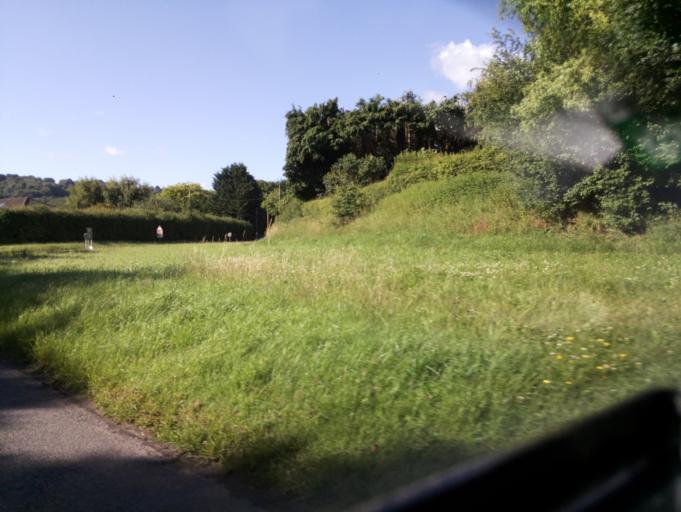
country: GB
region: England
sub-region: Herefordshire
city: Walford
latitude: 51.8902
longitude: -2.5890
